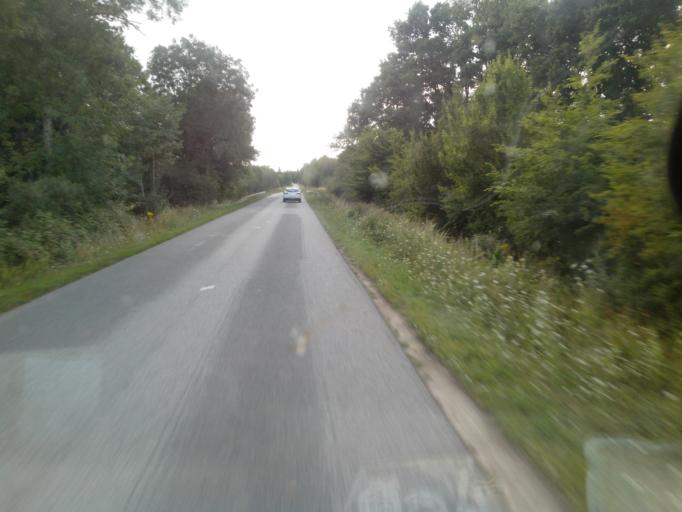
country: FR
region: Brittany
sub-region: Departement du Morbihan
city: Mauron
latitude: 48.0694
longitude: -2.2322
